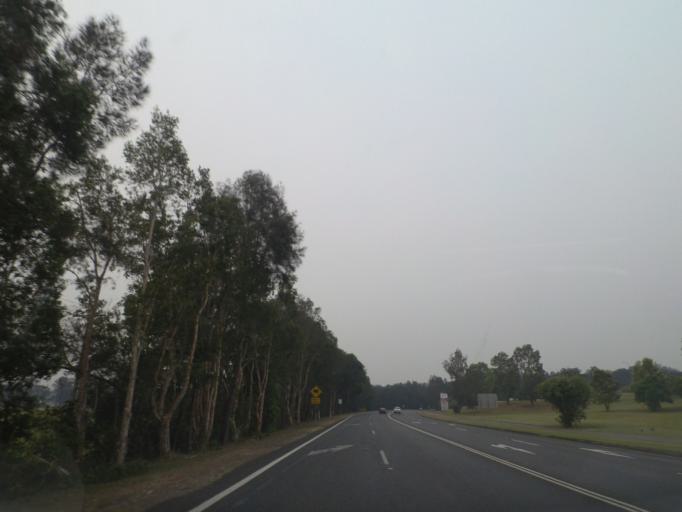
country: AU
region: New South Wales
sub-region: Coffs Harbour
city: Toormina
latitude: -30.3251
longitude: 153.0990
